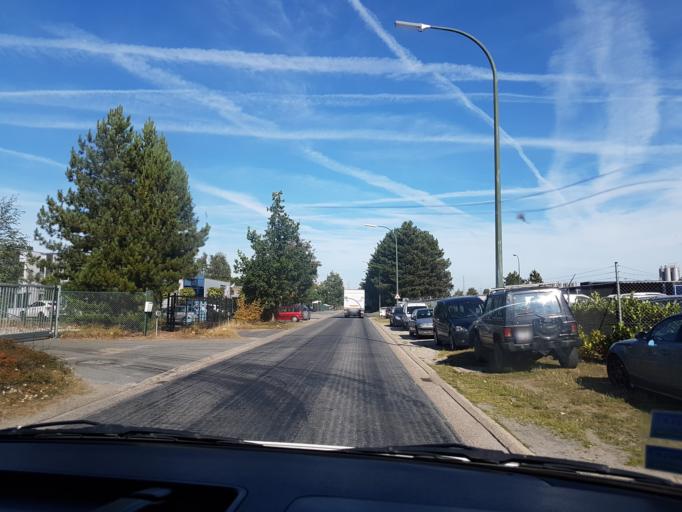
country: BE
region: Flanders
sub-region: Provincie Limburg
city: Overpelt
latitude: 51.2194
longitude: 5.3847
